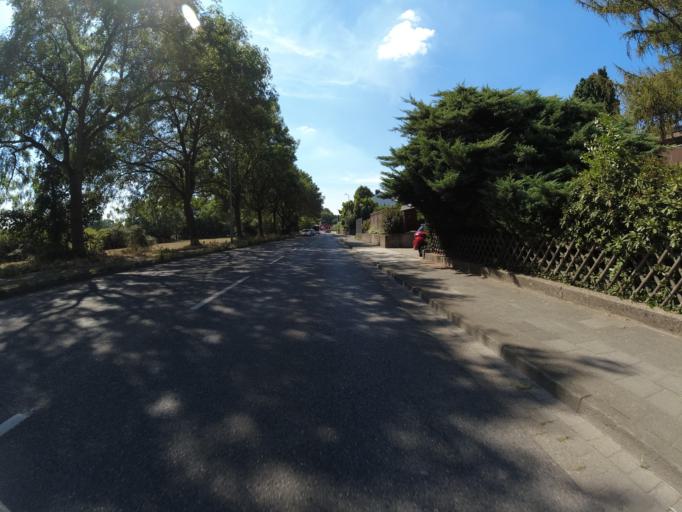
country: DE
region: North Rhine-Westphalia
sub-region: Regierungsbezirk Dusseldorf
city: Moers
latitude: 51.4911
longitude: 6.6749
